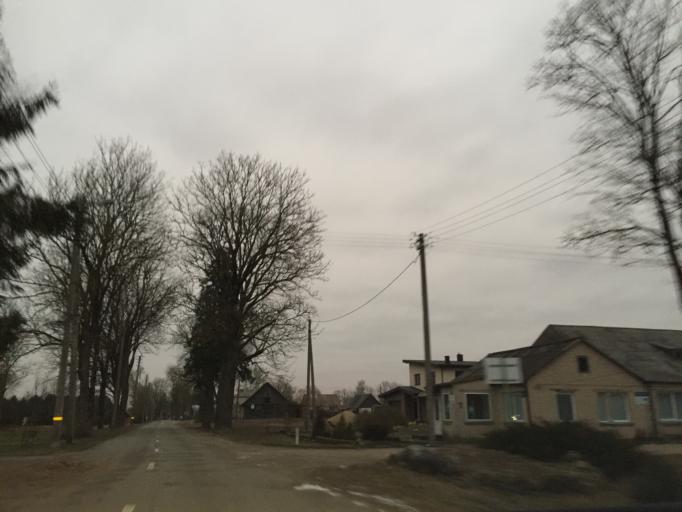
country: LT
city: Zagare
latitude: 56.3418
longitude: 23.3026
